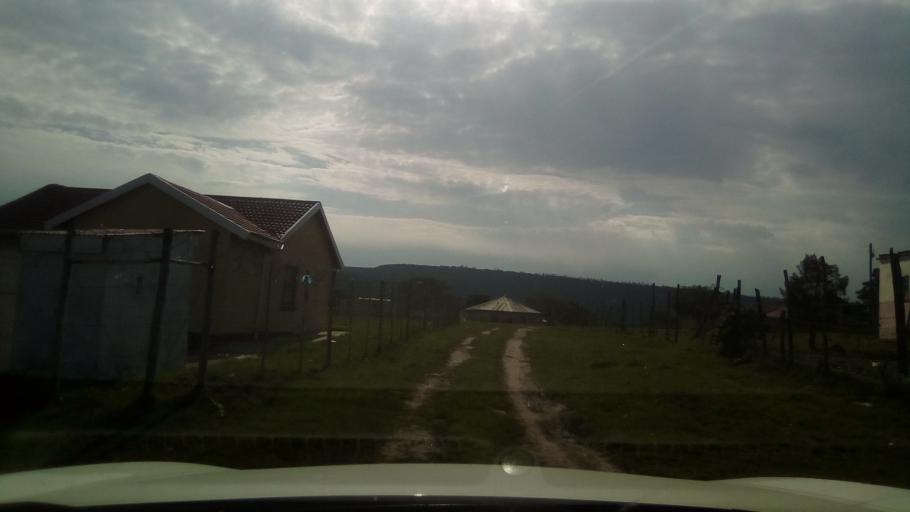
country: ZA
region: Eastern Cape
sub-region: Buffalo City Metropolitan Municipality
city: Bhisho
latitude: -32.9867
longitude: 27.2659
